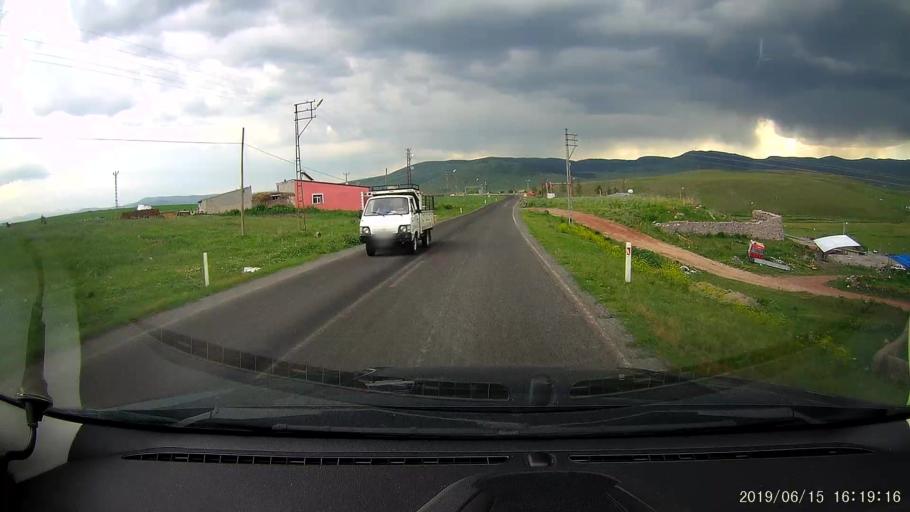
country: TR
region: Ardahan
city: Hanak
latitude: 41.2303
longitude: 42.8510
